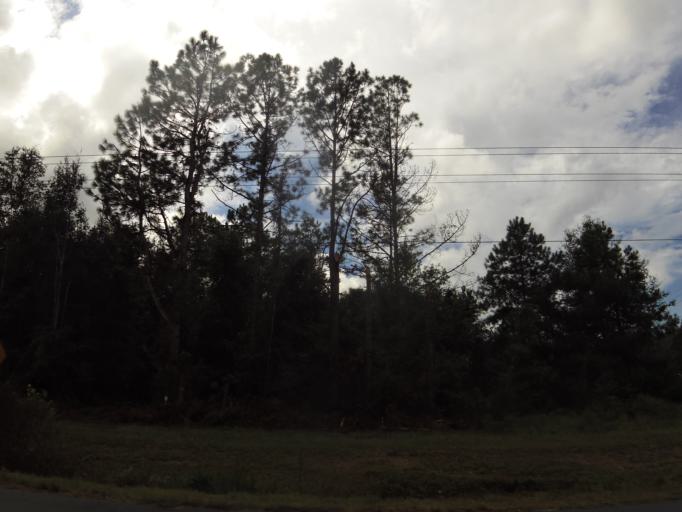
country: US
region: Florida
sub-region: Clay County
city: Middleburg
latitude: 30.0944
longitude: -81.9499
